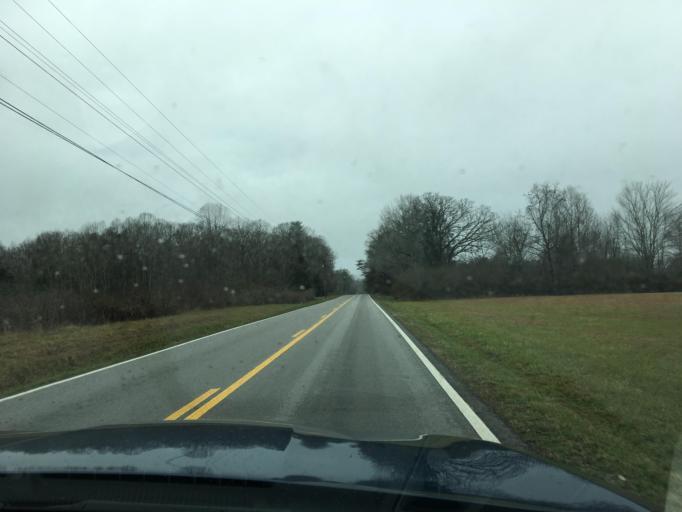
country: US
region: Tennessee
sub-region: Rhea County
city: Spring City
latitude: 35.7504
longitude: -84.8470
